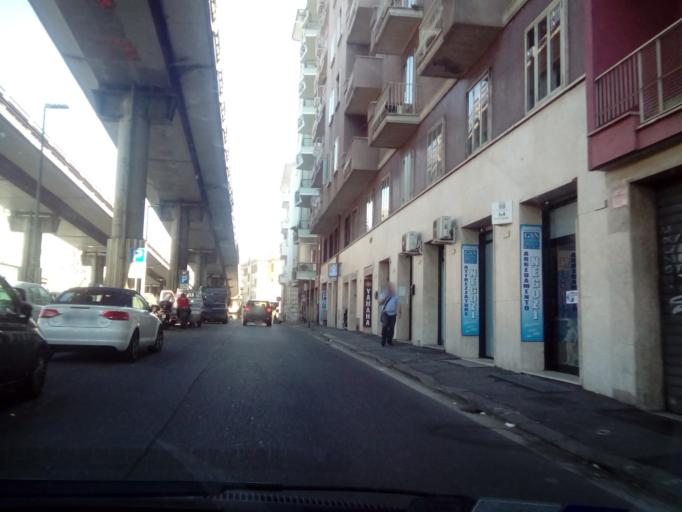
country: IT
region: Latium
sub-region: Citta metropolitana di Roma Capitale
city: Rome
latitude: 41.8911
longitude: 12.5223
